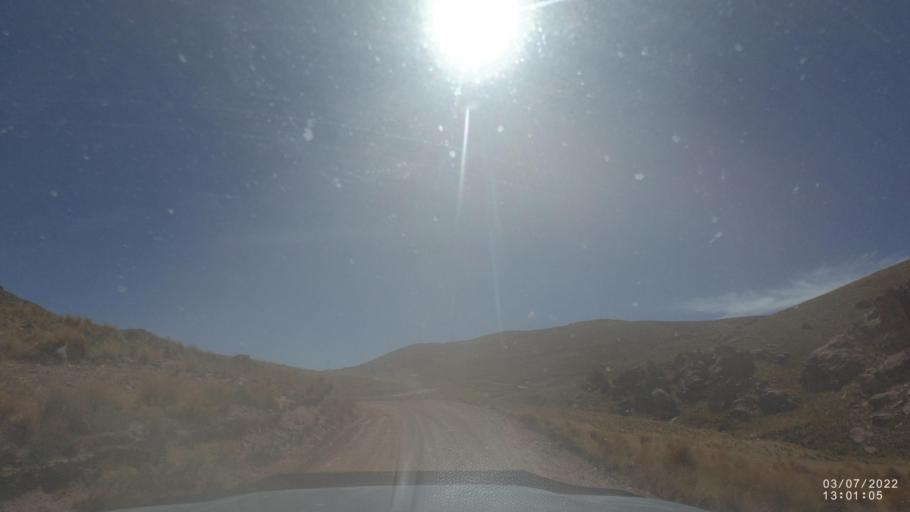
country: BO
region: Cochabamba
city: Colchani
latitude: -17.7108
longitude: -66.6904
